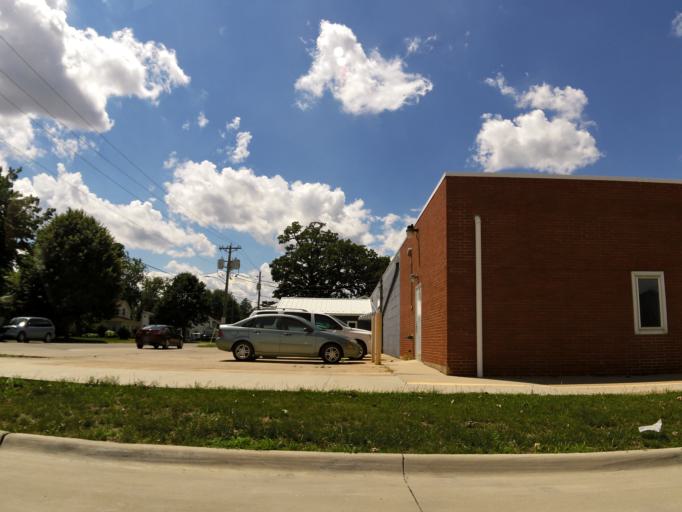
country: US
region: Iowa
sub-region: Buchanan County
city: Independence
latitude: 42.4680
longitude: -91.8954
